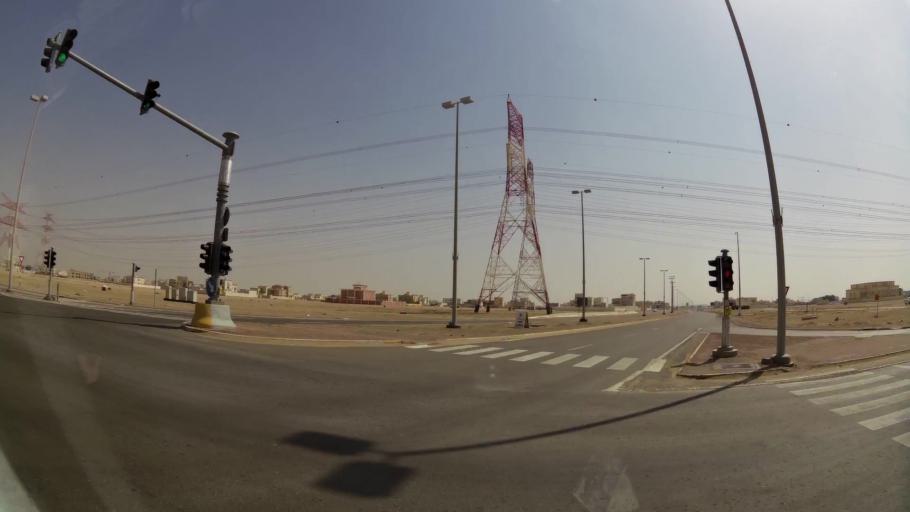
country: AE
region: Abu Dhabi
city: Abu Dhabi
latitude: 24.3082
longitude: 54.5752
